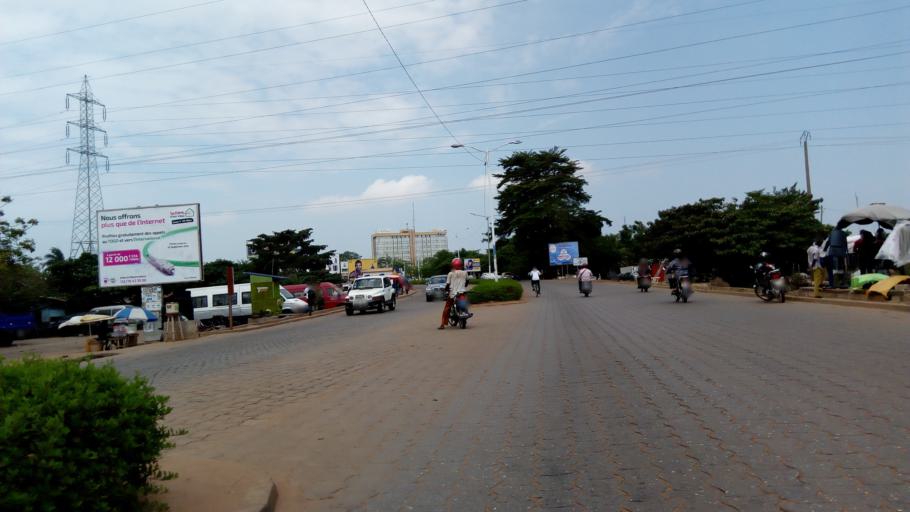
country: TG
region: Maritime
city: Lome
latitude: 6.1946
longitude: 1.2065
